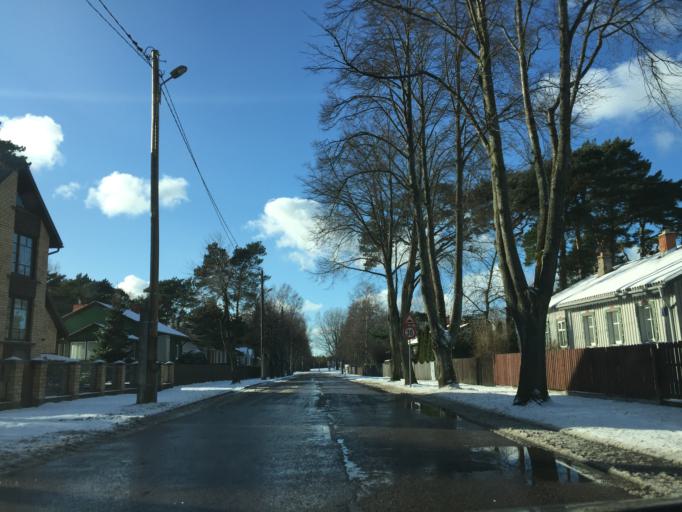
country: LV
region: Ventspils
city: Ventspils
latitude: 57.3883
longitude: 21.5395
